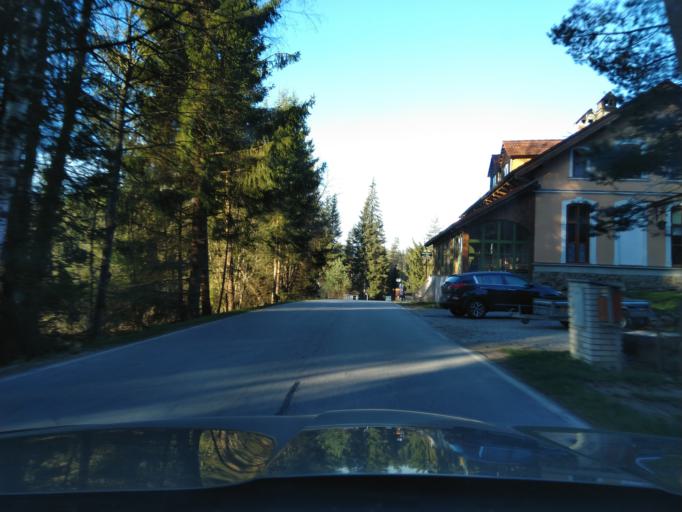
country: CZ
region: Jihocesky
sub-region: Okres Prachatice
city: Volary
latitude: 48.9089
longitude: 13.8294
